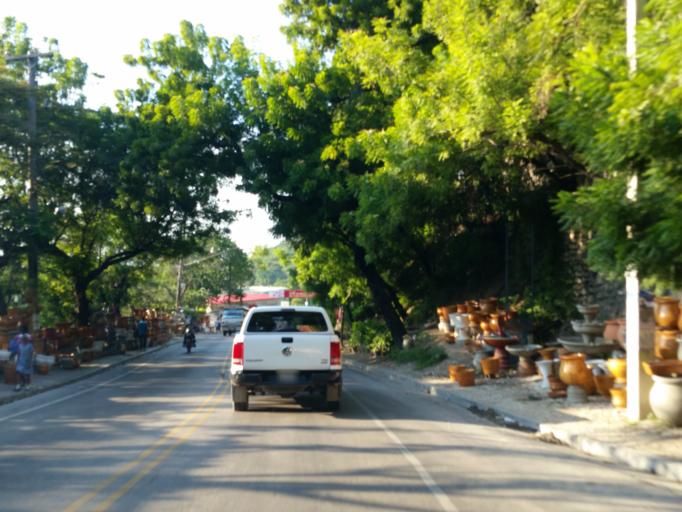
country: HT
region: Ouest
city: Delmas 73
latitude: 18.5295
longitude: -72.3000
